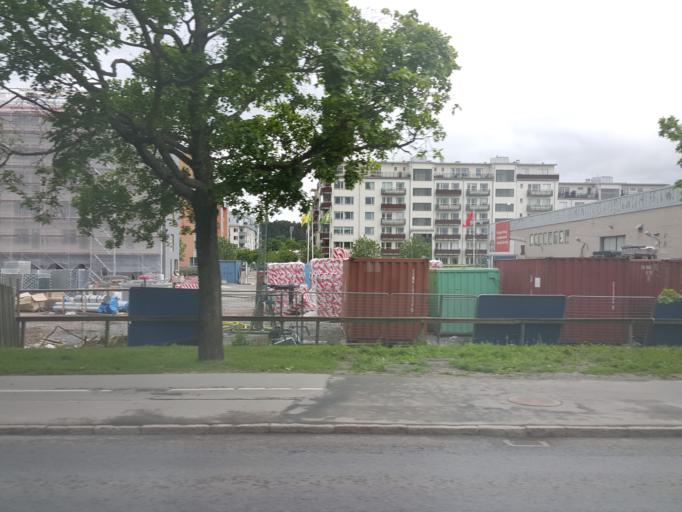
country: SE
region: Uppsala
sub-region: Uppsala Kommun
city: Uppsala
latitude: 59.8518
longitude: 17.6560
